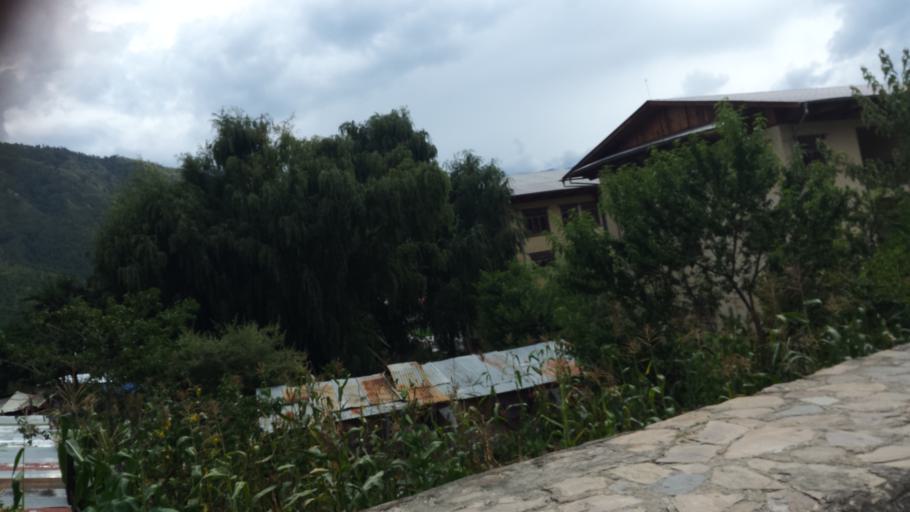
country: BT
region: Thimphu
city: Thimphu
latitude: 27.4719
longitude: 89.6319
